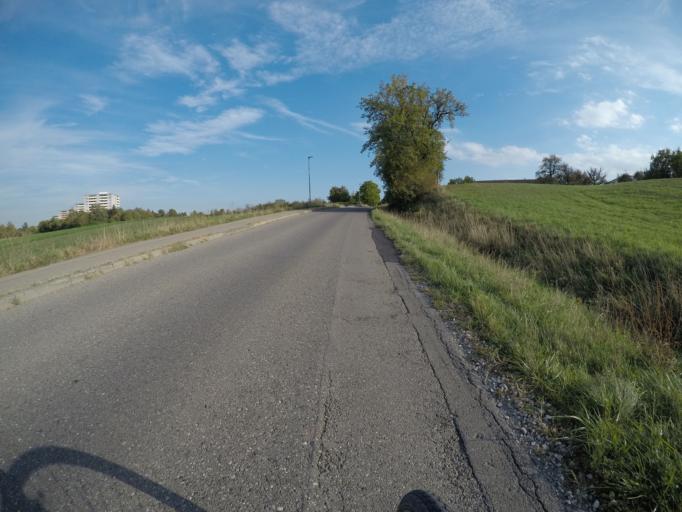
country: DE
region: Baden-Wuerttemberg
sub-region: Tuebingen Region
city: Sickenhausen
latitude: 48.5238
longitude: 9.1992
